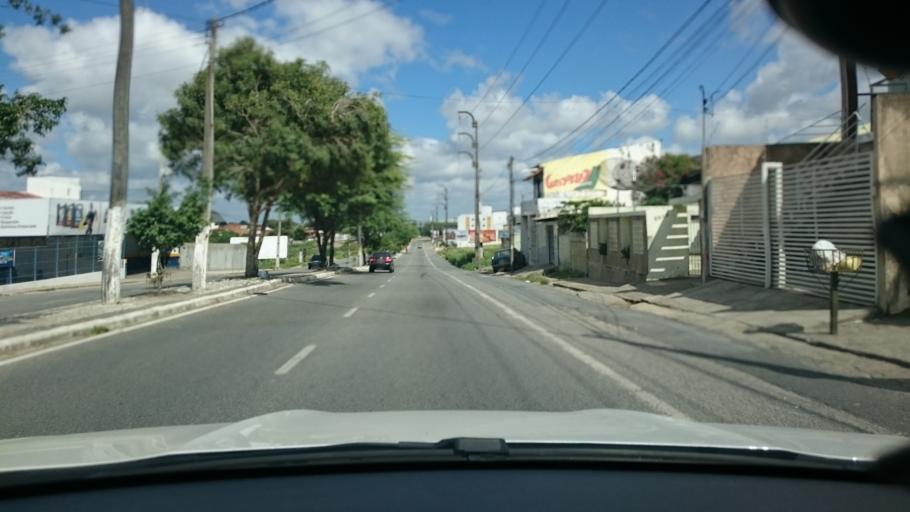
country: BR
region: Paraiba
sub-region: Campina Grande
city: Campina Grande
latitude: -7.2298
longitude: -35.9064
